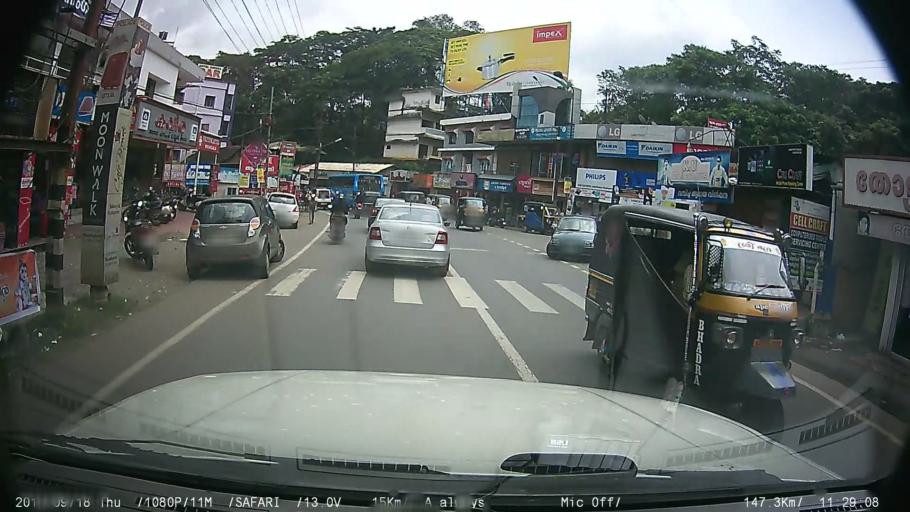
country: IN
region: Kerala
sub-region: Ernakulam
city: Muvattupula
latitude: 9.9845
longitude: 76.5785
